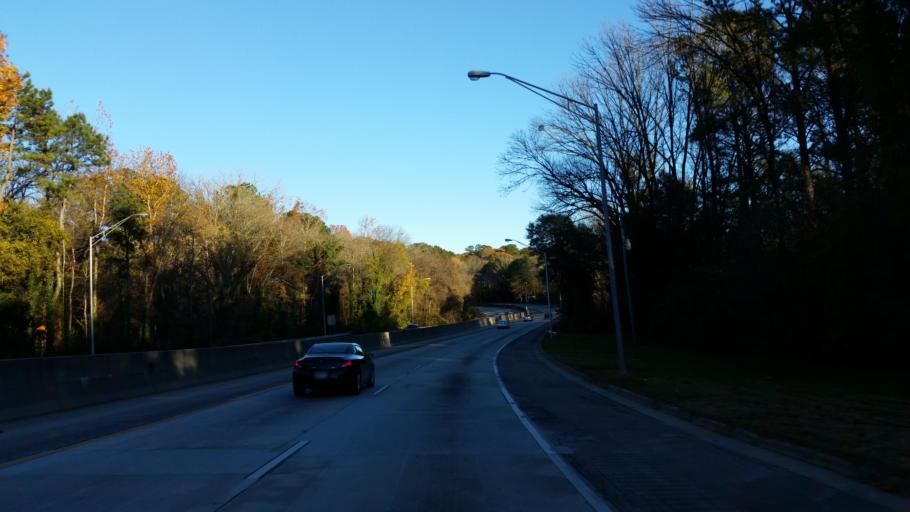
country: US
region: Georgia
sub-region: Fulton County
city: East Point
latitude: 33.6981
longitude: -84.4674
